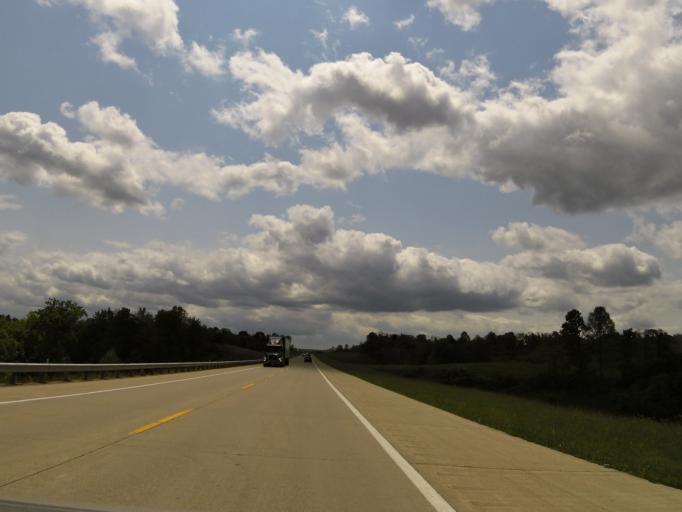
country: US
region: Ohio
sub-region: Athens County
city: Athens
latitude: 39.2654
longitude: -82.0841
